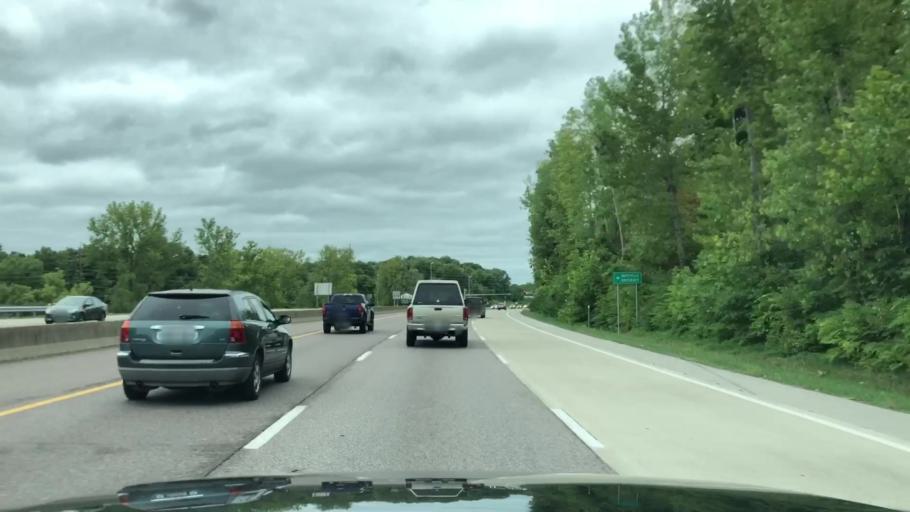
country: US
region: Missouri
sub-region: Saint Louis County
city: Manchester
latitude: 38.6522
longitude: -90.5071
